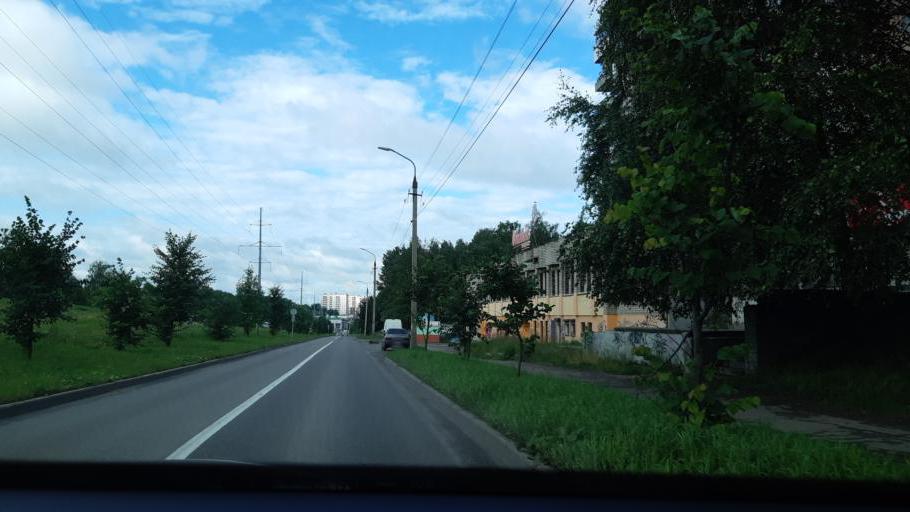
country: RU
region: Smolensk
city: Smolensk
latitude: 54.7638
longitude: 32.0894
